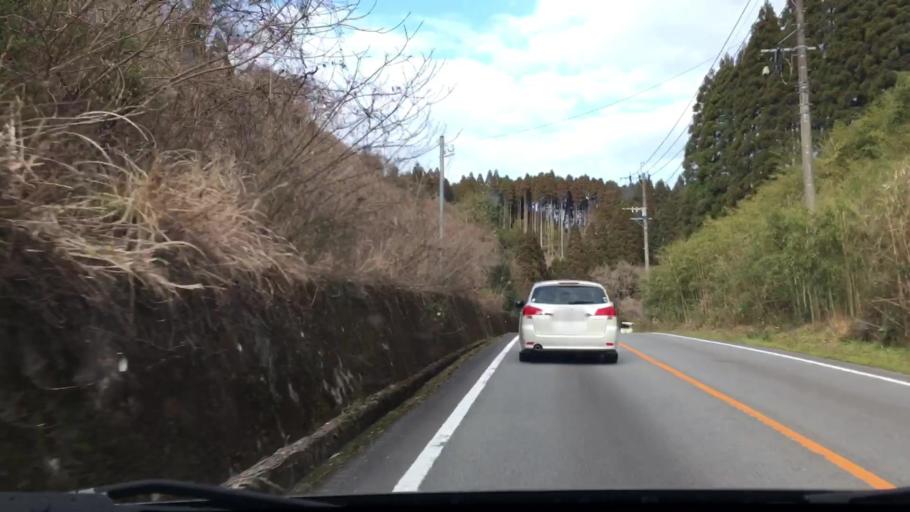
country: JP
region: Miyazaki
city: Nichinan
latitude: 31.7211
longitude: 131.3261
